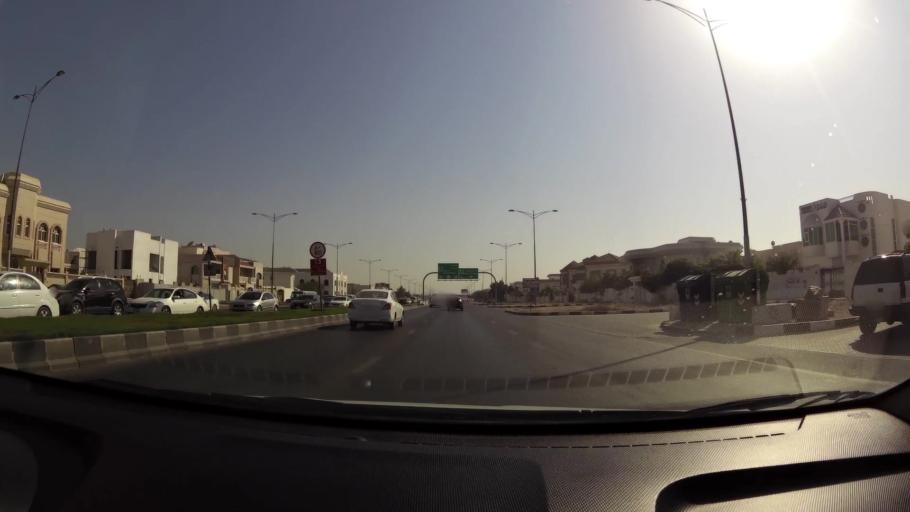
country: AE
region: Ash Shariqah
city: Sharjah
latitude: 25.3531
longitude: 55.4379
